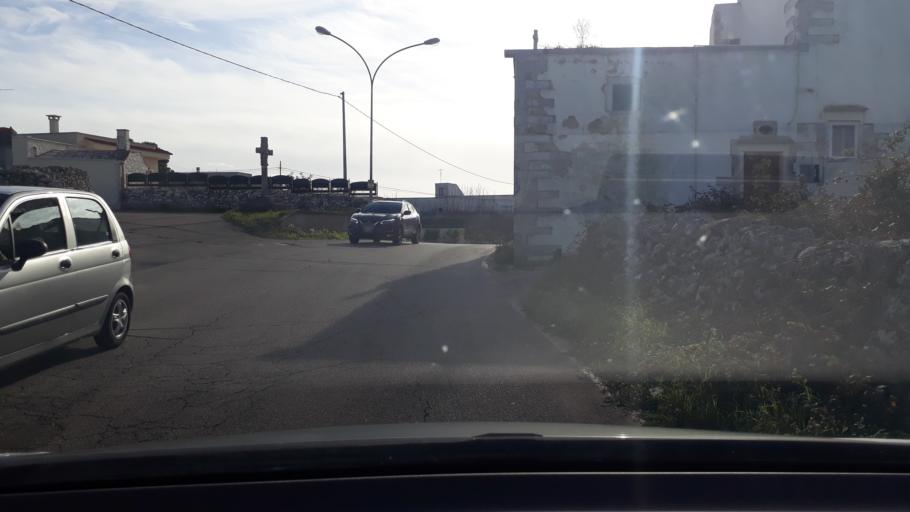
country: IT
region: Apulia
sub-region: Provincia di Taranto
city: Martina Franca
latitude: 40.6927
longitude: 17.3488
